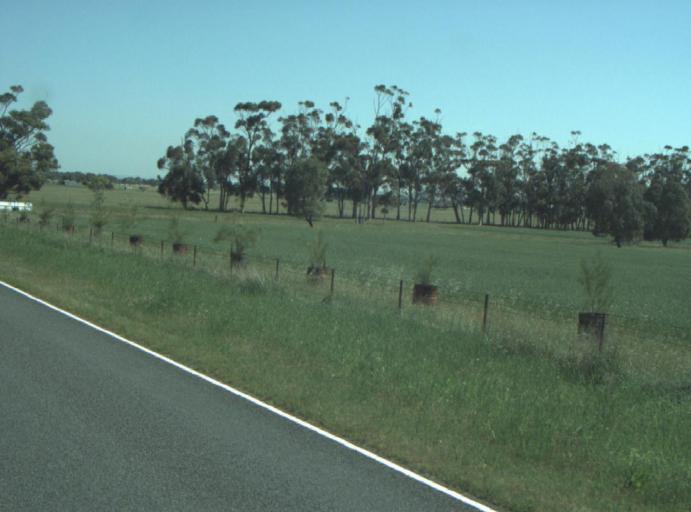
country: AU
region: Victoria
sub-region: Greater Geelong
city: Lara
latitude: -37.9708
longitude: 144.4057
